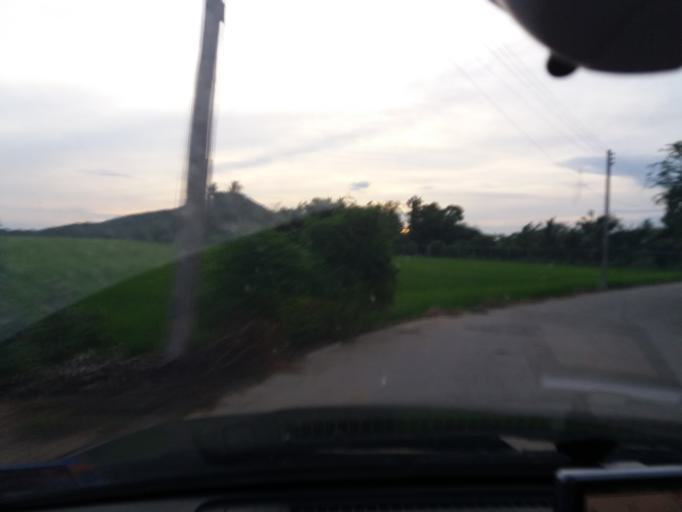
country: TH
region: Suphan Buri
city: Doembang Nangbuat
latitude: 14.8294
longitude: 100.1364
